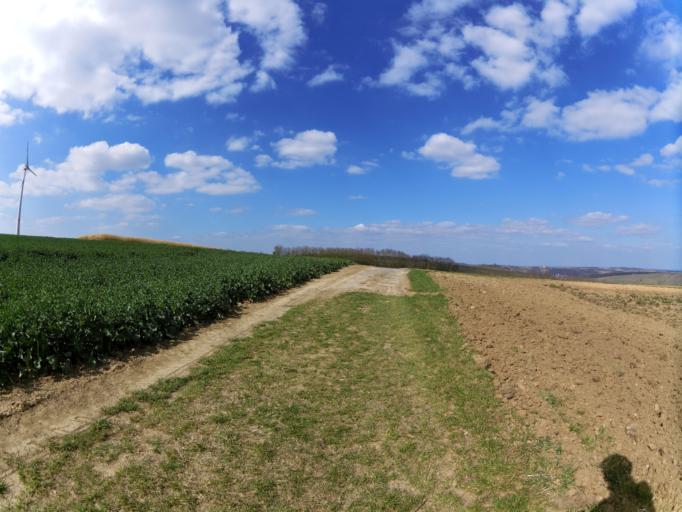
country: DE
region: Bavaria
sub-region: Regierungsbezirk Unterfranken
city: Dettelbach
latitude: 49.8302
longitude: 10.1713
